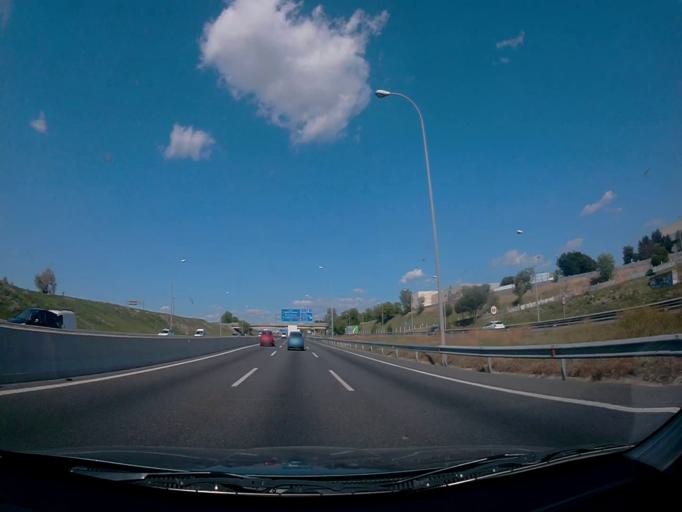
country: ES
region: Madrid
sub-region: Provincia de Madrid
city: Puente de Vallecas
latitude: 40.3632
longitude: -3.6660
